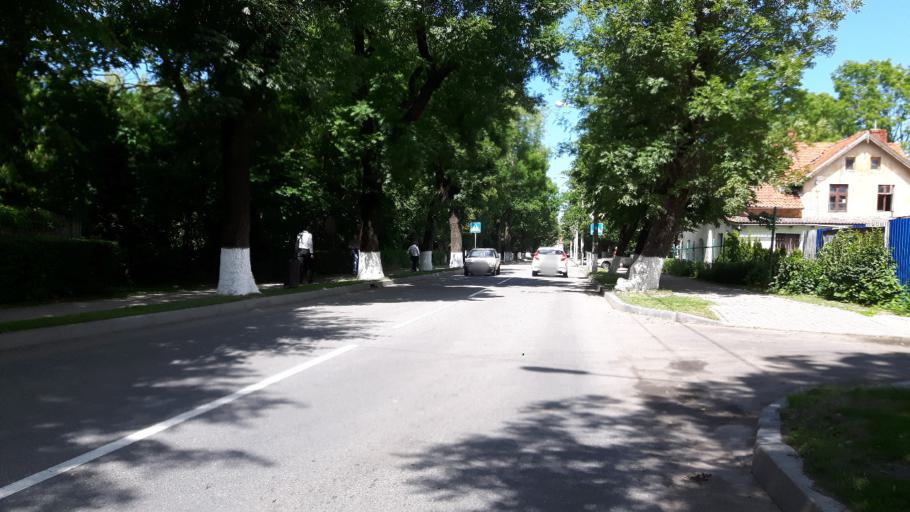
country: RU
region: Kaliningrad
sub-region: Zelenogradskiy Rayon
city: Zelenogradsk
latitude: 54.9554
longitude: 20.4712
